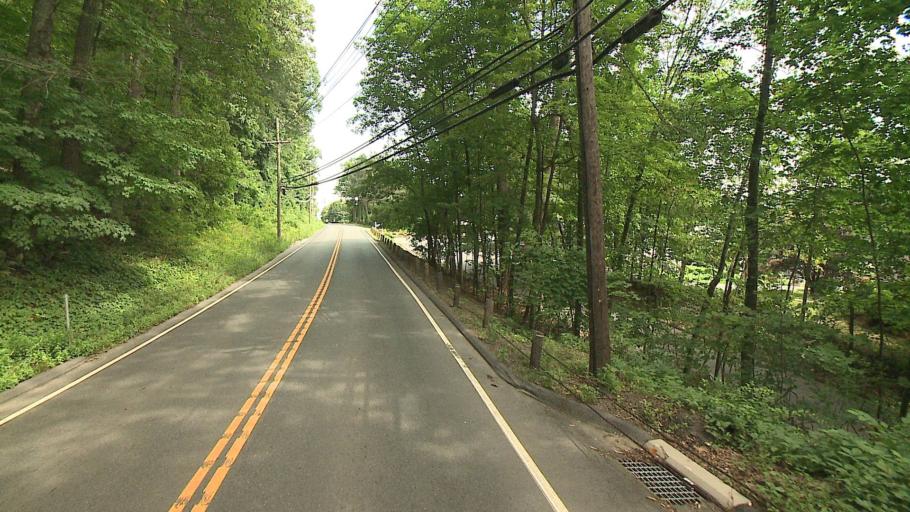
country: US
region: New York
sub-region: Putnam County
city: Putnam Lake
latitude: 41.4825
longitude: -73.4644
